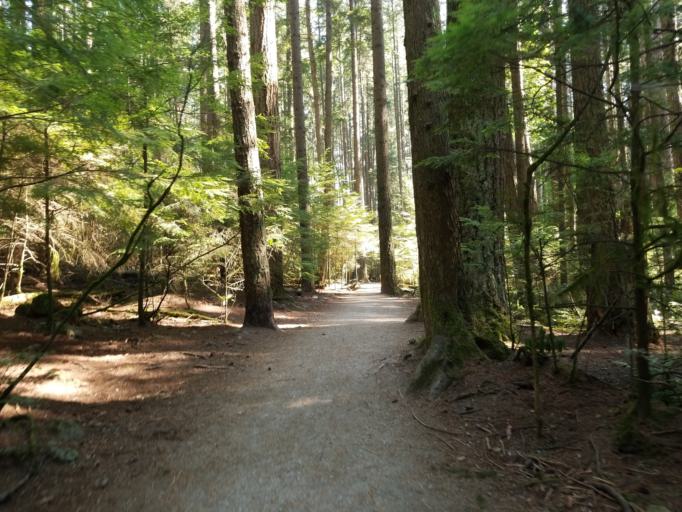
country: CA
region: British Columbia
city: West End
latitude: 49.2520
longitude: -123.2177
